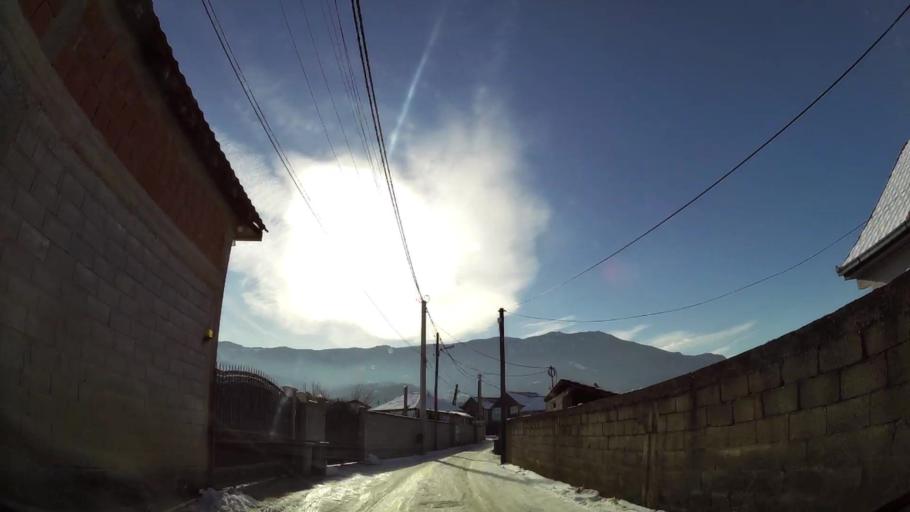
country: MK
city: Grchec
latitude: 41.9906
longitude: 21.3260
